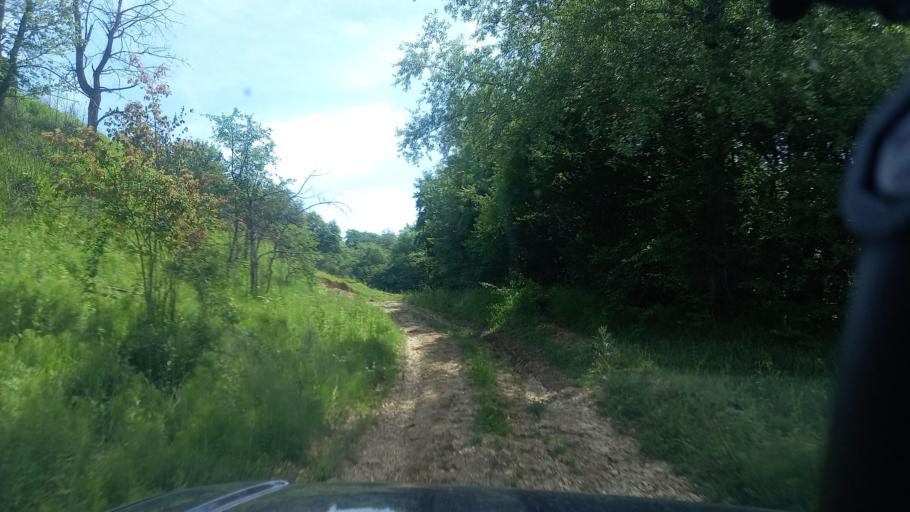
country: RU
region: Karachayevo-Cherkesiya
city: Kurdzhinovo
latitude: 44.1405
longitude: 41.0718
